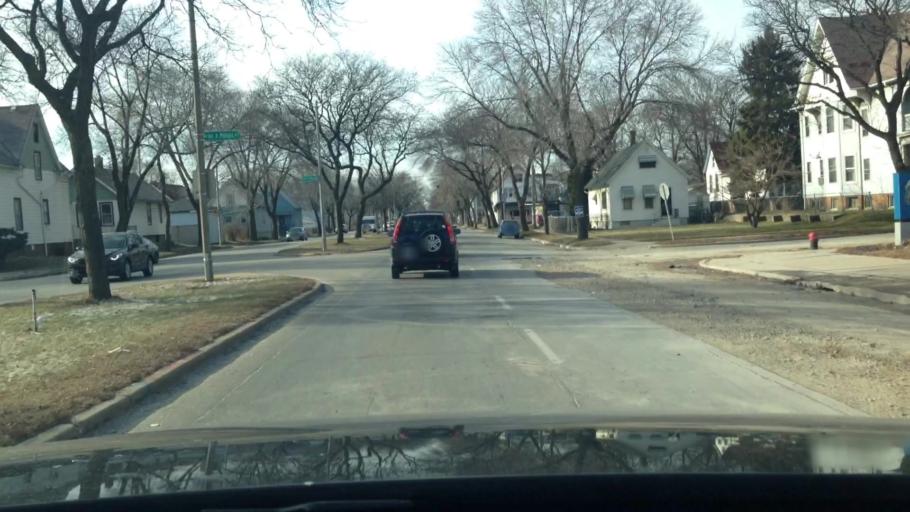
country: US
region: Wisconsin
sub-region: Milwaukee County
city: Shorewood
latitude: 43.0712
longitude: -87.9150
